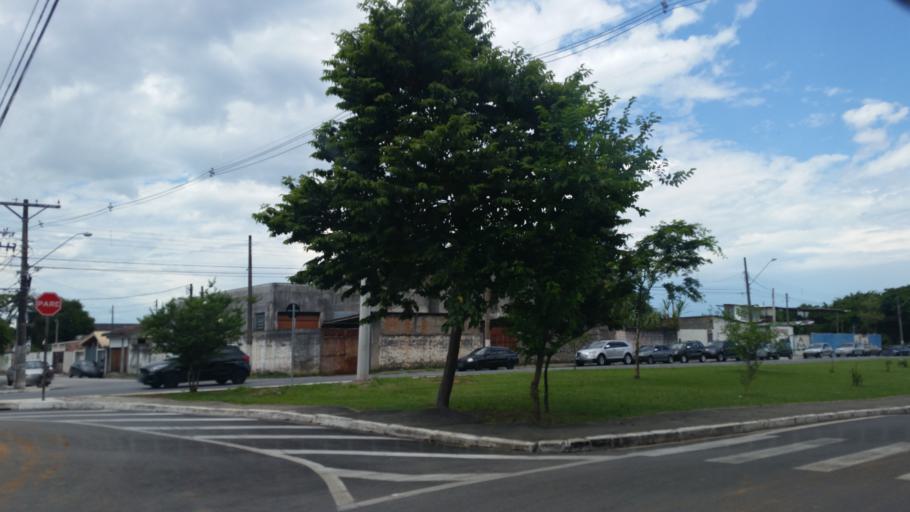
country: BR
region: Sao Paulo
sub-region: Taubate
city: Taubate
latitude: -23.0177
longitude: -45.5855
